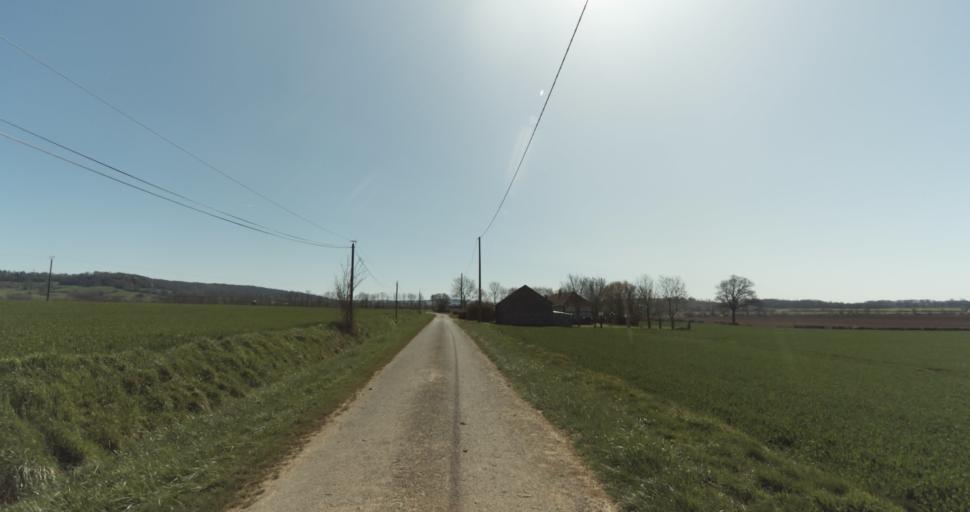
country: FR
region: Lower Normandy
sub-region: Departement du Calvados
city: Saint-Pierre-sur-Dives
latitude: 49.0040
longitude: 0.0202
